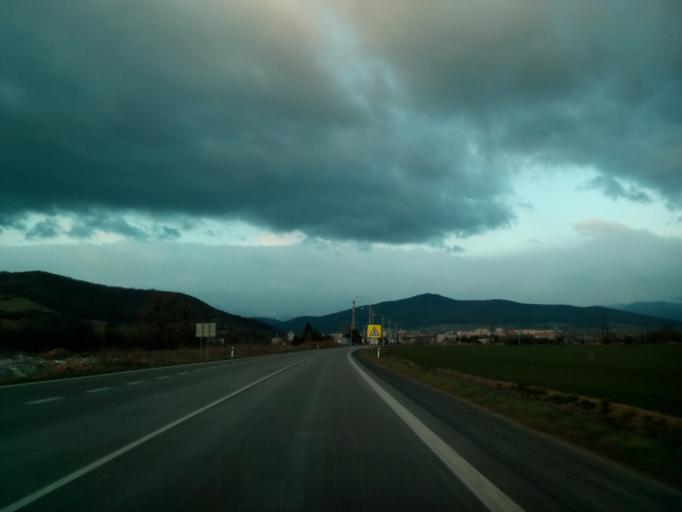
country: SK
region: Kosicky
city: Roznava
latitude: 48.6346
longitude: 20.5077
